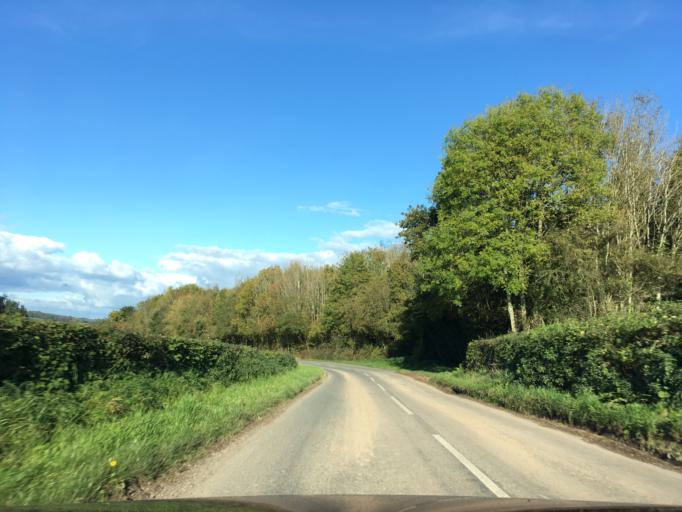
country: GB
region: England
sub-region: Herefordshire
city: Clifford
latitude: 52.0963
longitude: -3.1088
